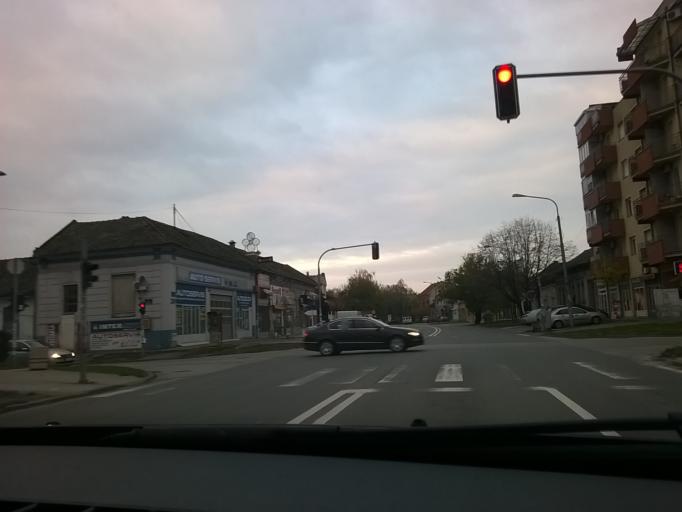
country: RS
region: Autonomna Pokrajina Vojvodina
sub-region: Juznobacki Okrug
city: Novi Sad
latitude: 45.2642
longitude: 19.8438
